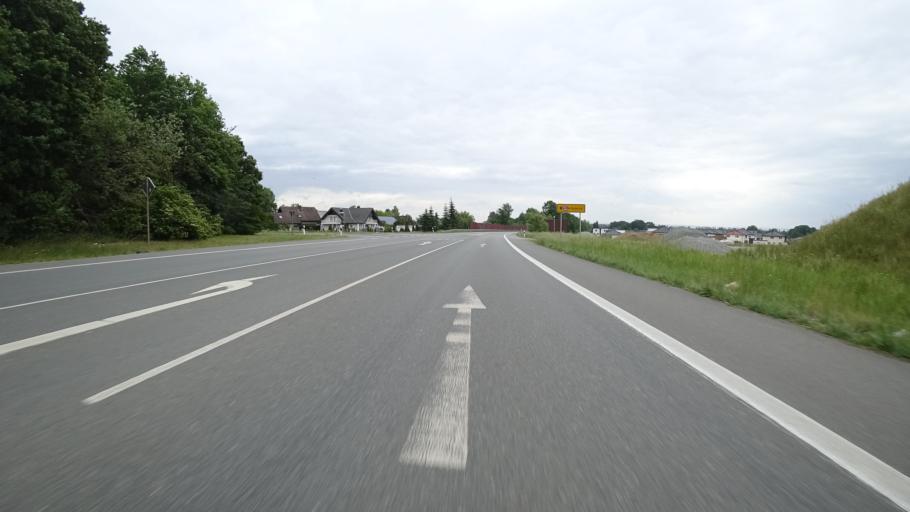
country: DE
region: North Rhine-Westphalia
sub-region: Regierungsbezirk Detmold
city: Delbruck
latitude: 51.7671
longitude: 8.5465
